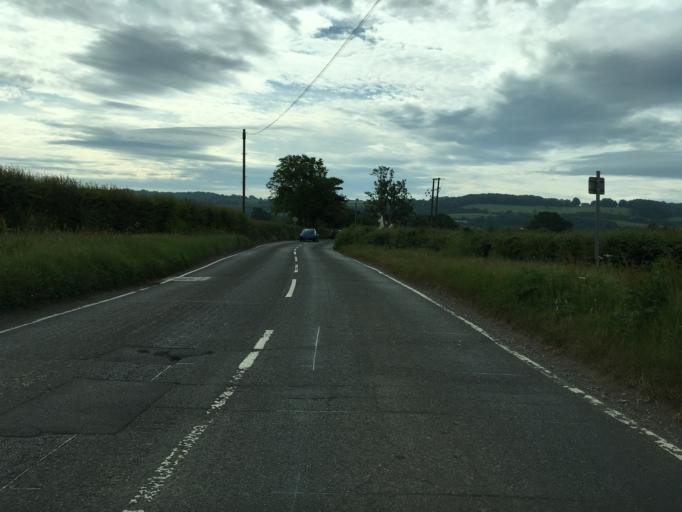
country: GB
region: England
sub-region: North Somerset
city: Portishead
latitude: 51.4729
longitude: -2.7682
